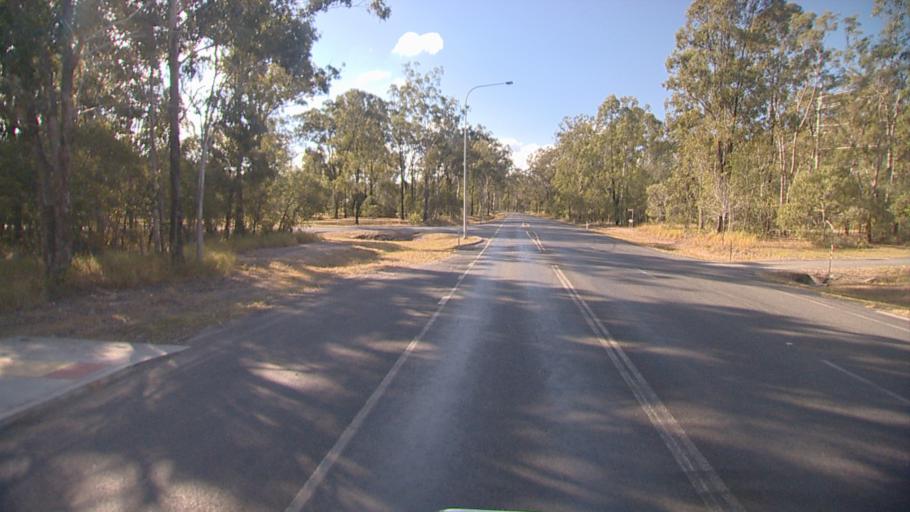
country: AU
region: Queensland
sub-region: Logan
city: North Maclean
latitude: -27.7614
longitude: 152.9865
